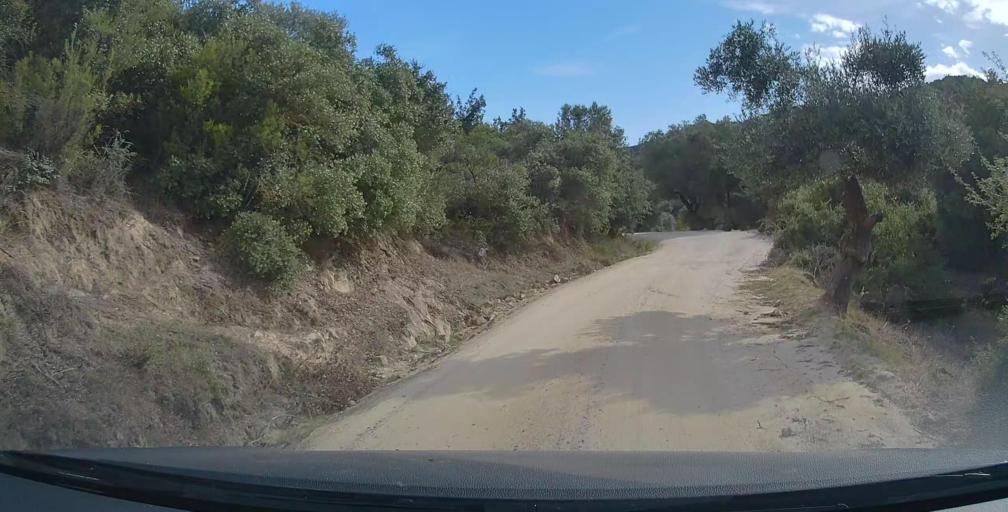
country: GR
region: Central Macedonia
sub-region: Nomos Chalkidikis
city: Sykia
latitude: 40.0173
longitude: 23.9385
